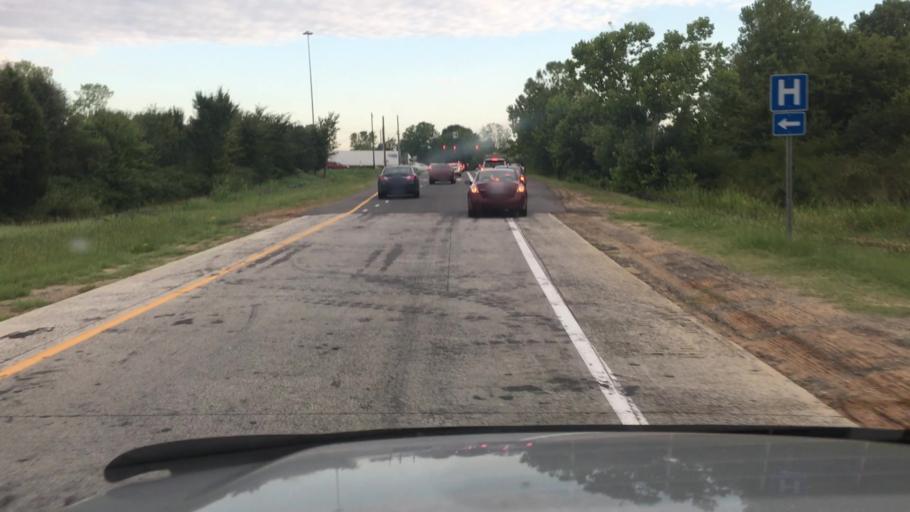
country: US
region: North Carolina
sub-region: Mecklenburg County
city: Pineville
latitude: 35.1410
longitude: -80.9295
